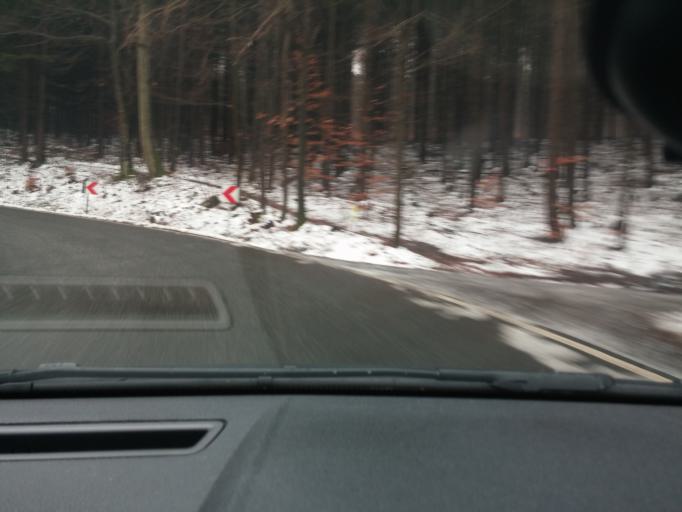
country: DE
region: Hesse
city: Michelstadt
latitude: 49.6903
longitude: 9.0409
